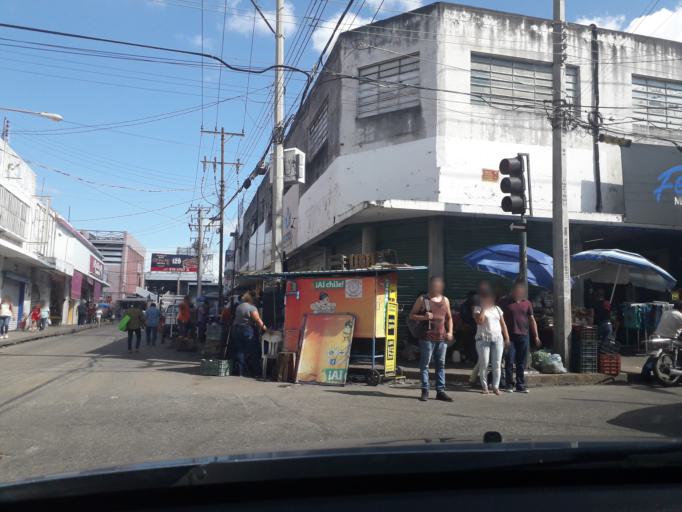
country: MX
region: Yucatan
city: Merida
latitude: 20.9634
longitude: -89.6226
